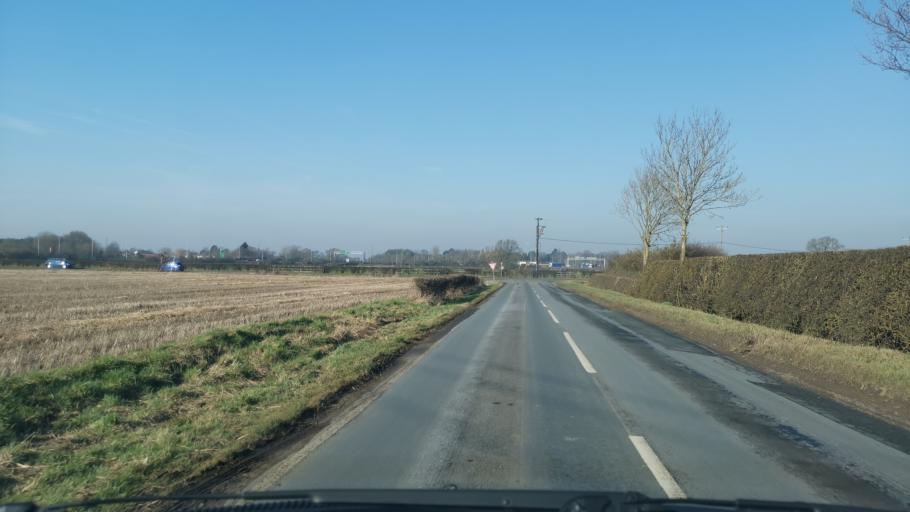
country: GB
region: England
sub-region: City of York
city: Murton
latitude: 53.9864
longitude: -1.0167
